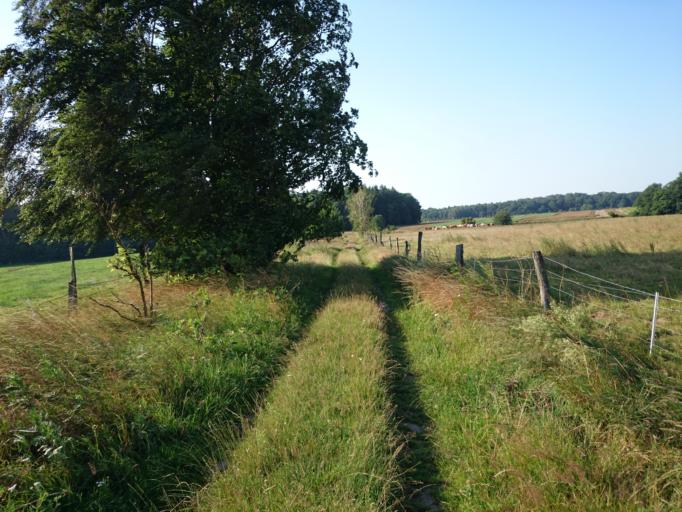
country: DE
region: Mecklenburg-Vorpommern
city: Tessin
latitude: 54.0275
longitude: 12.4025
